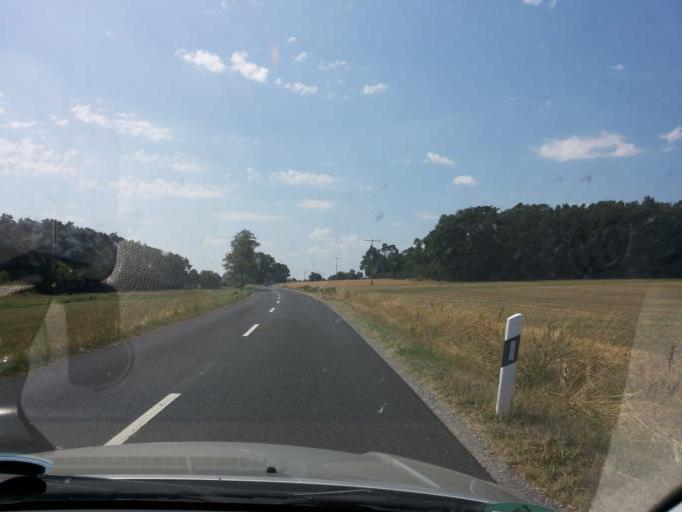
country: DE
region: Bavaria
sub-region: Regierungsbezirk Mittelfranken
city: Hagenbuchach
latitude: 49.5221
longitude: 10.7373
